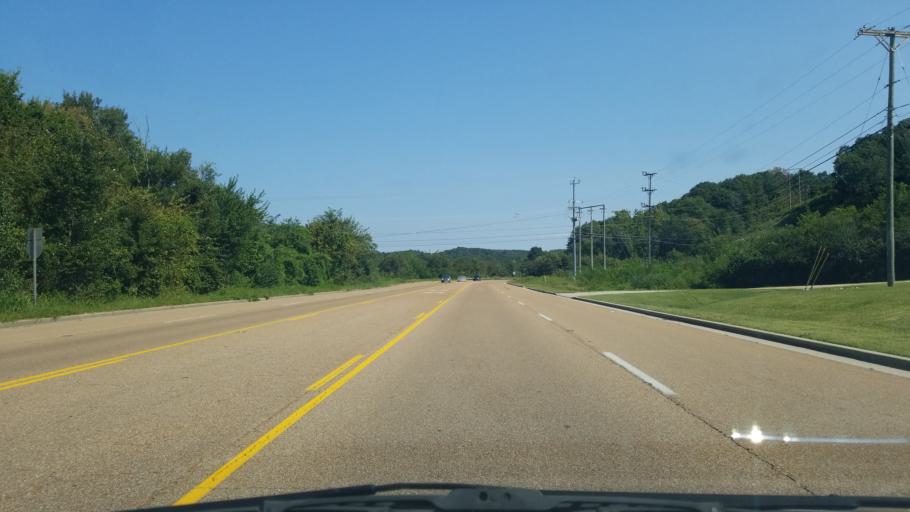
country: US
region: Tennessee
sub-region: Hamilton County
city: Harrison
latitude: 35.0613
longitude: -85.1271
